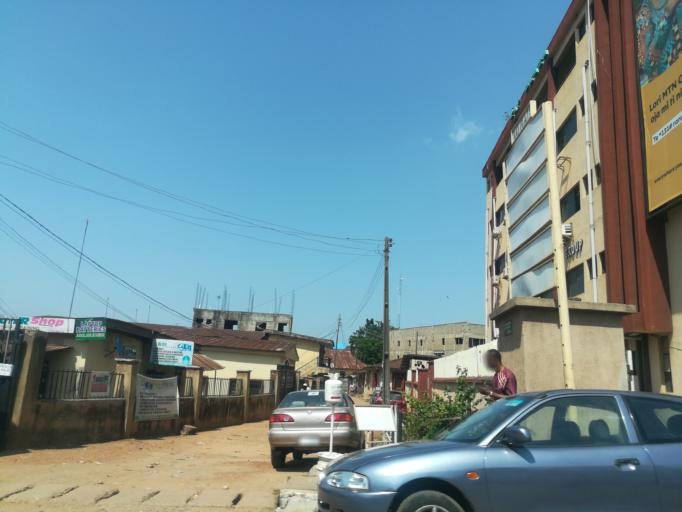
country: NG
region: Ogun
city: Abeokuta
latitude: 7.1352
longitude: 3.3386
